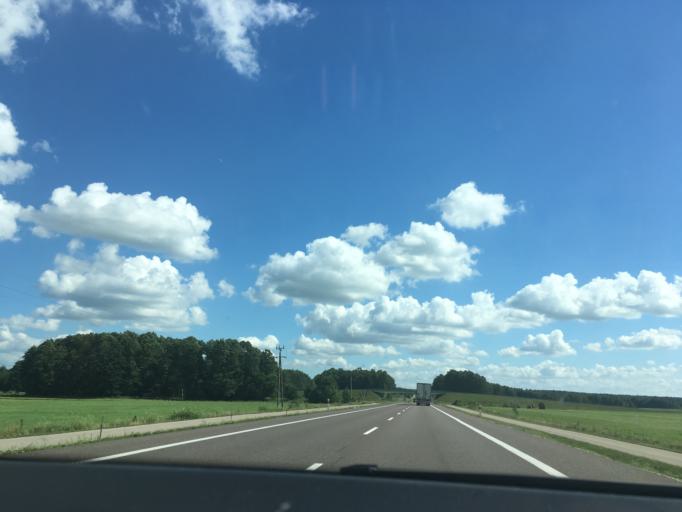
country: PL
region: Podlasie
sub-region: Powiat augustowski
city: Augustow
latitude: 53.7539
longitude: 23.0884
